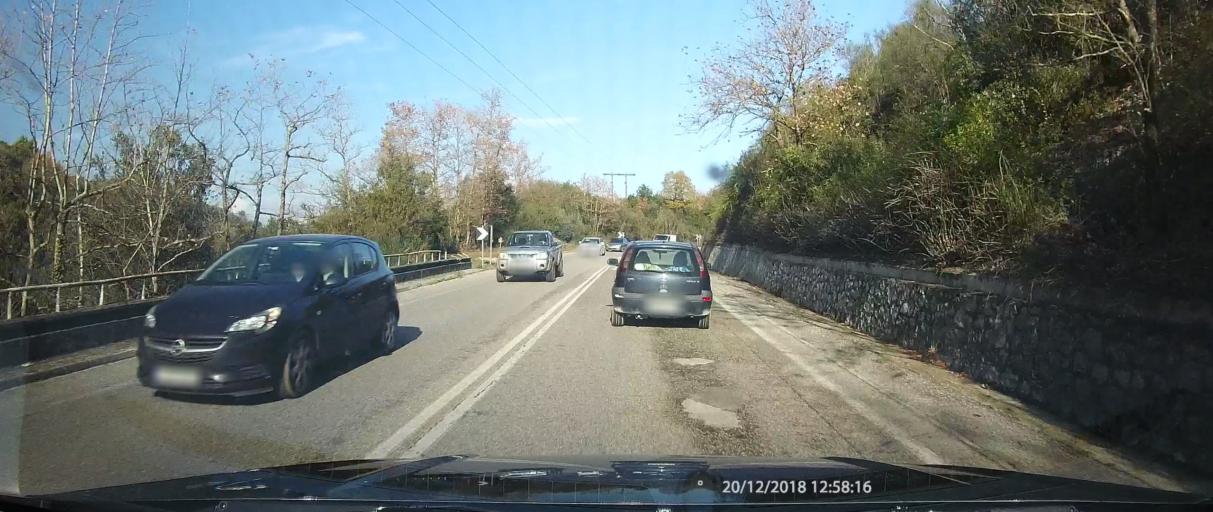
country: GR
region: West Greece
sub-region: Nomos Aitolias kai Akarnanias
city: Pappadhatai
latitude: 38.5350
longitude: 21.3754
